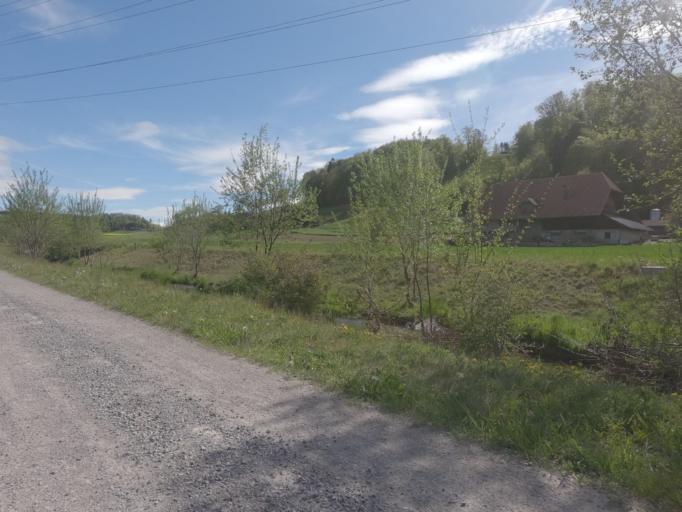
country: CH
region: Bern
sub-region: Bern-Mittelland District
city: Vechigen
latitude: 46.9393
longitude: 7.5512
